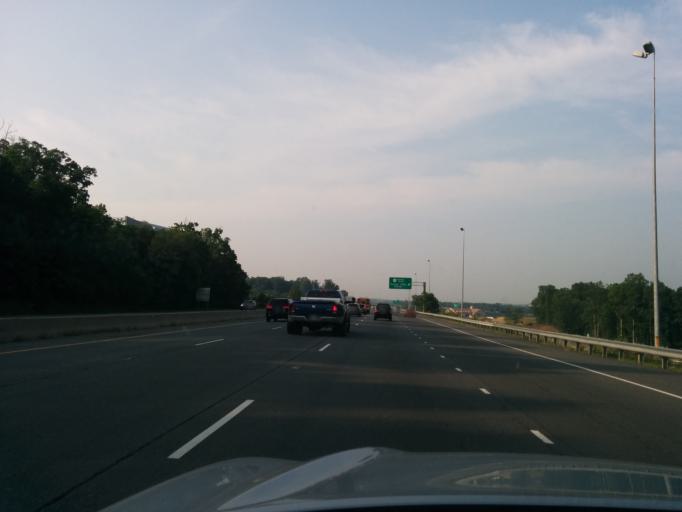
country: US
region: Virginia
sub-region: Loudoun County
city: Dulles Town Center
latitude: 39.0380
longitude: -77.4315
